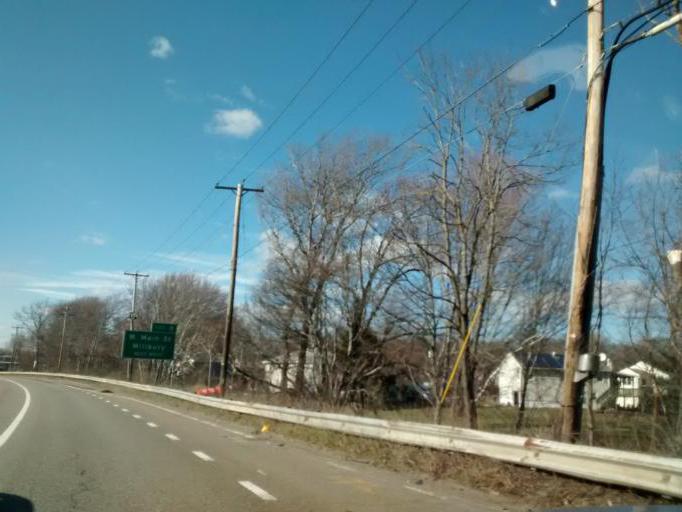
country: US
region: Massachusetts
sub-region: Worcester County
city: Millbury
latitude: 42.1847
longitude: -71.7633
